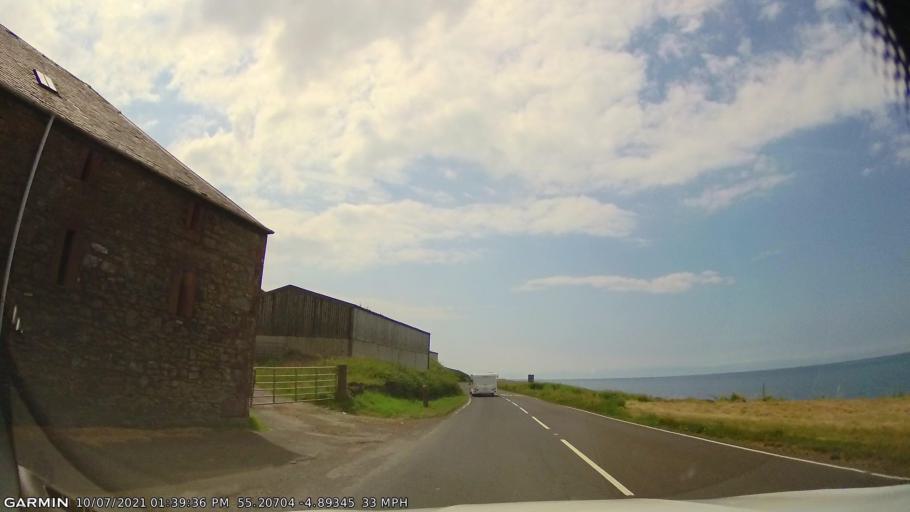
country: GB
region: Scotland
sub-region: South Ayrshire
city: Girvan
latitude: 55.2070
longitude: -4.8934
